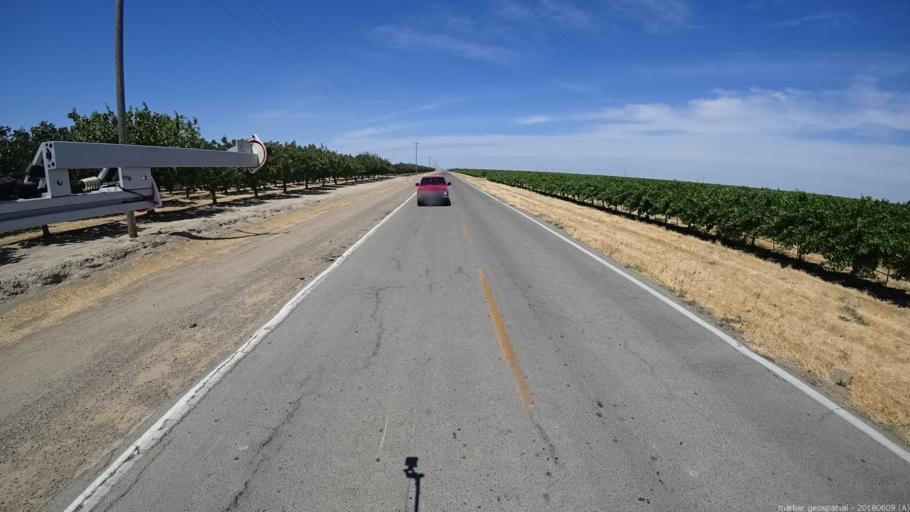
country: US
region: California
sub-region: Fresno County
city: Firebaugh
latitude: 36.9527
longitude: -120.3224
